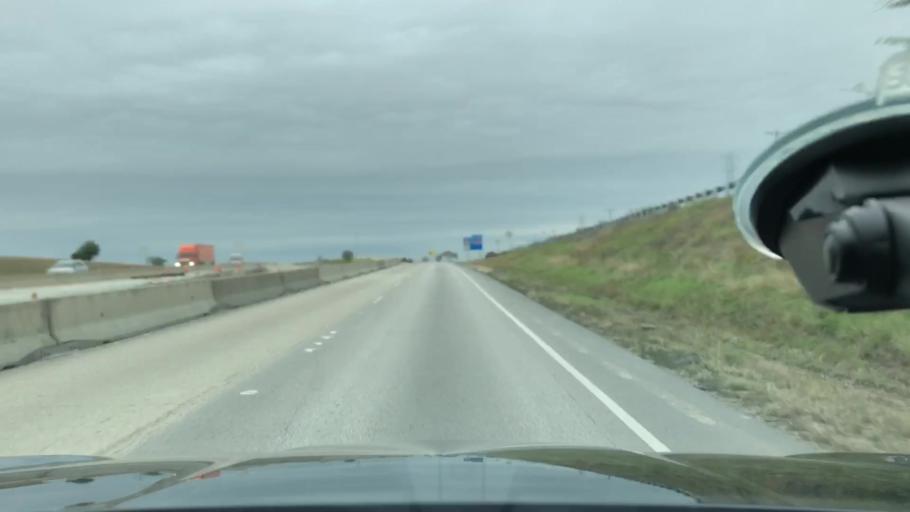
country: US
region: Texas
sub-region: Ellis County
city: Waxahachie
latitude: 32.3579
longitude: -96.8548
